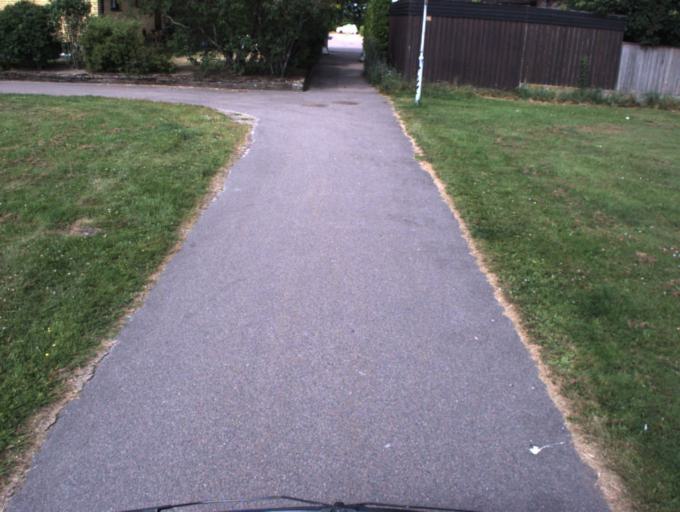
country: SE
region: Skane
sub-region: Helsingborg
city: Barslov
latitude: 56.0349
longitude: 12.8111
